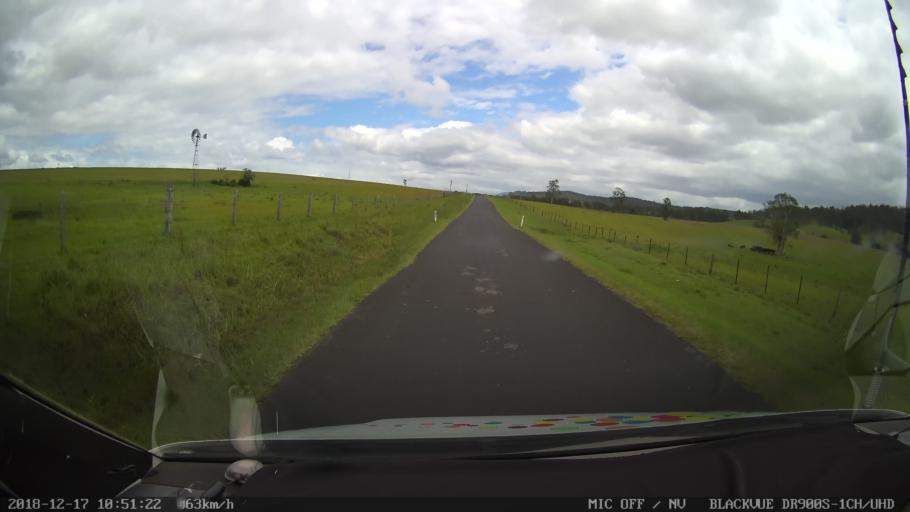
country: AU
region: New South Wales
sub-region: Tenterfield Municipality
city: Carrolls Creek
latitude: -28.8524
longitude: 152.5674
